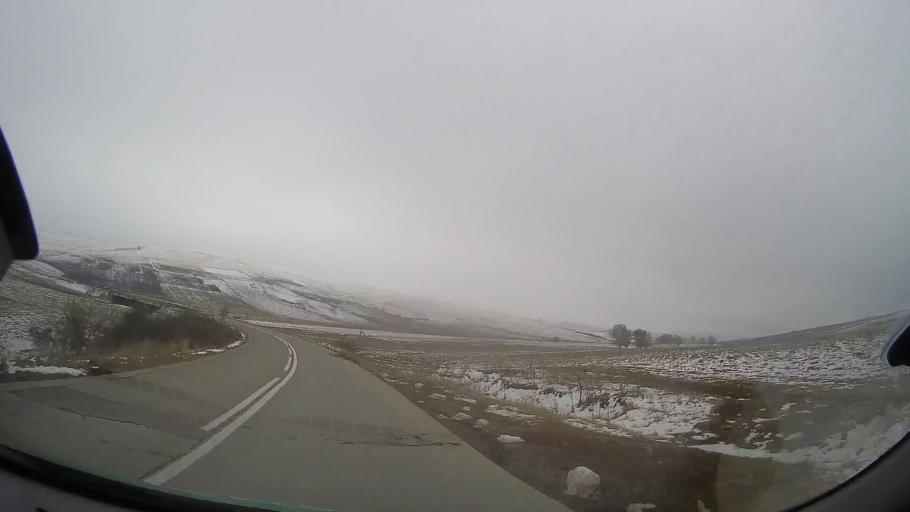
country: RO
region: Vaslui
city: Coroiesti
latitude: 46.2103
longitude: 27.4923
